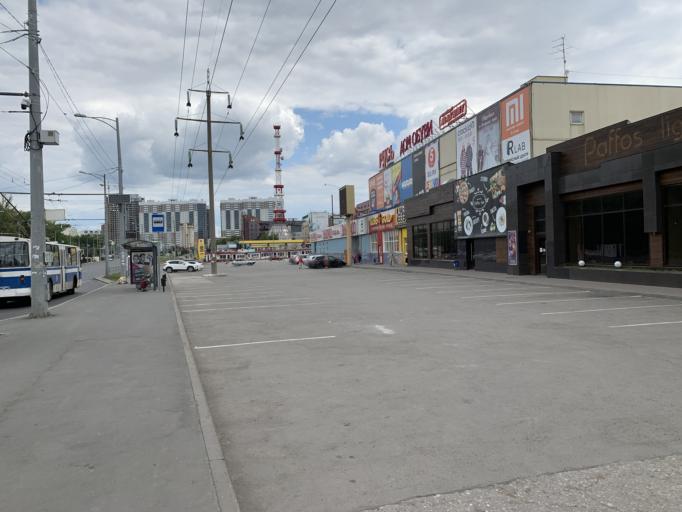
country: RU
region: Samara
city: Samara
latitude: 53.2125
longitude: 50.1805
